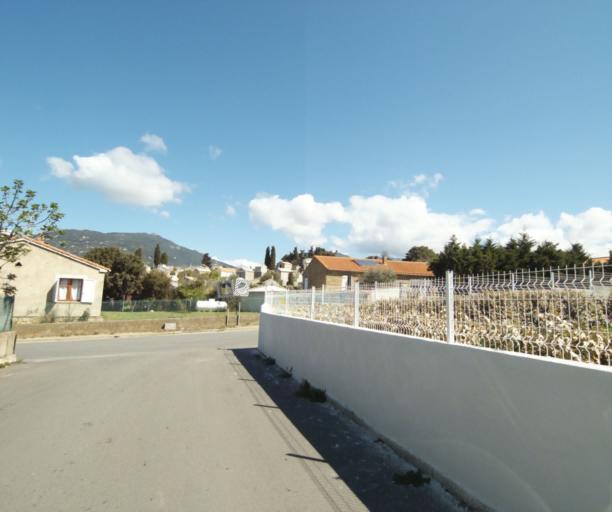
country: FR
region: Corsica
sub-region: Departement de la Corse-du-Sud
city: Propriano
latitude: 41.6776
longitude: 8.9128
